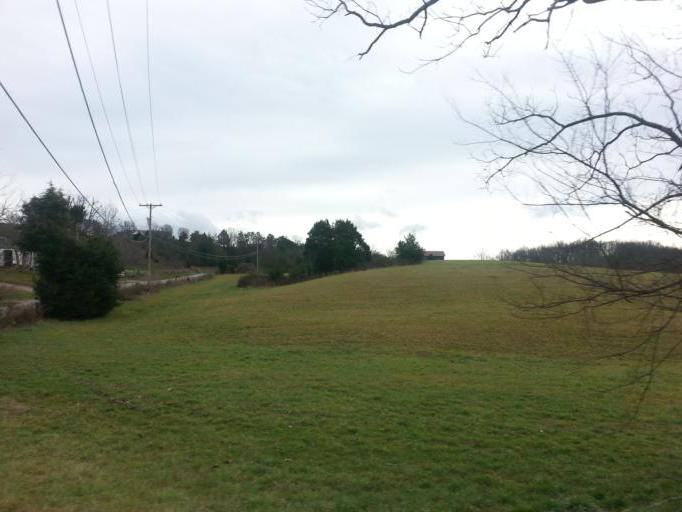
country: US
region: Tennessee
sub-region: Greene County
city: Greeneville
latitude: 36.1395
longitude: -82.8724
